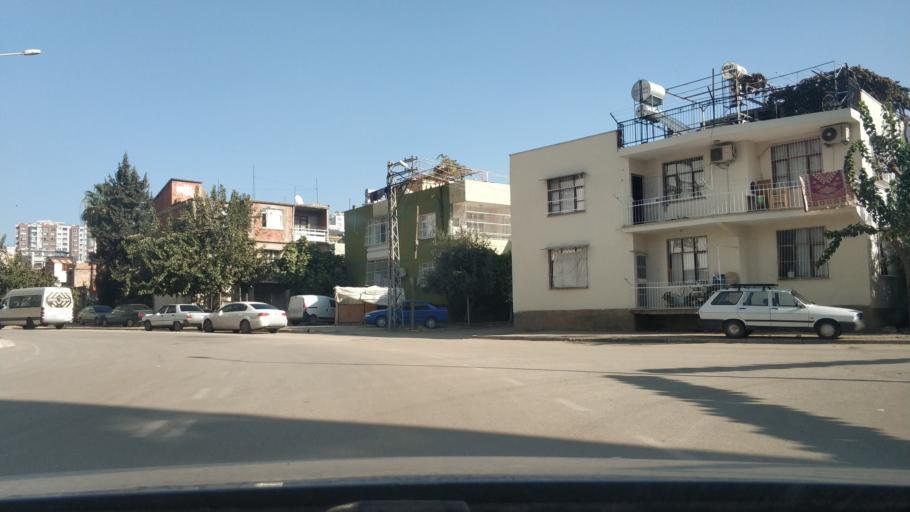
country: TR
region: Adana
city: Seyhan
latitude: 37.0188
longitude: 35.2913
